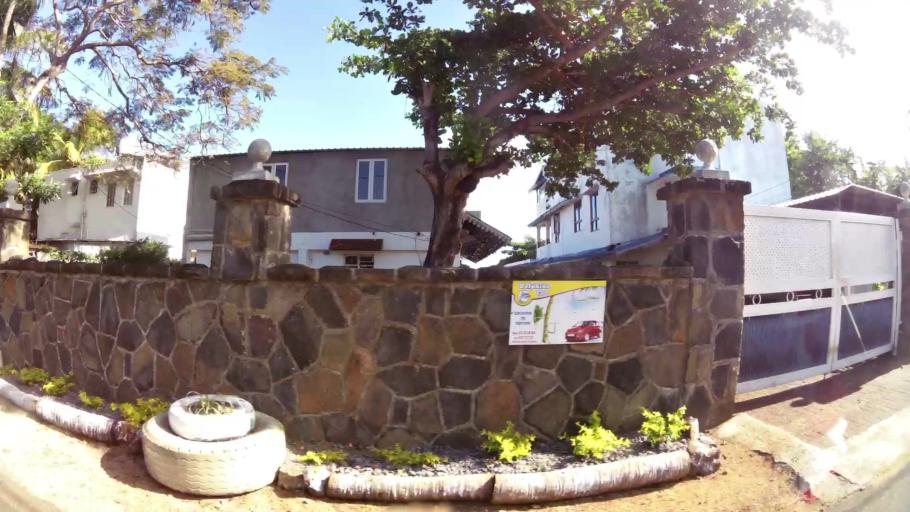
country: MU
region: Black River
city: Albion
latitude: -20.2031
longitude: 57.4041
